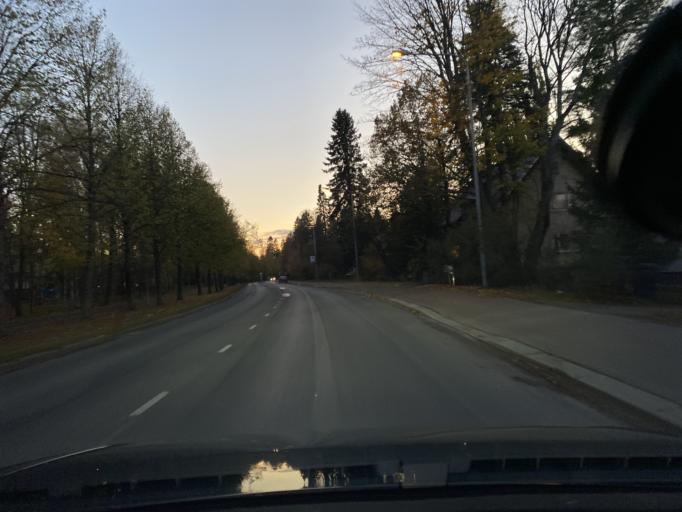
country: FI
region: Pirkanmaa
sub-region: Tampere
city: Tampere
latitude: 61.4727
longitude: 23.7575
